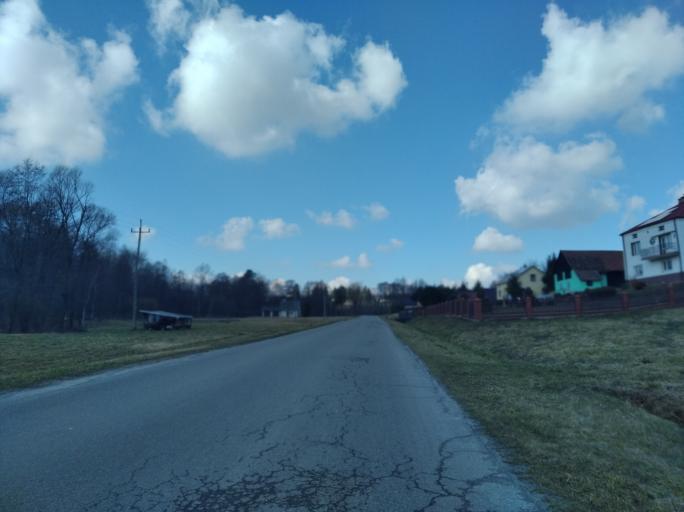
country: PL
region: Subcarpathian Voivodeship
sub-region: Powiat strzyzowski
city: Frysztak
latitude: 49.8702
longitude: 21.5313
